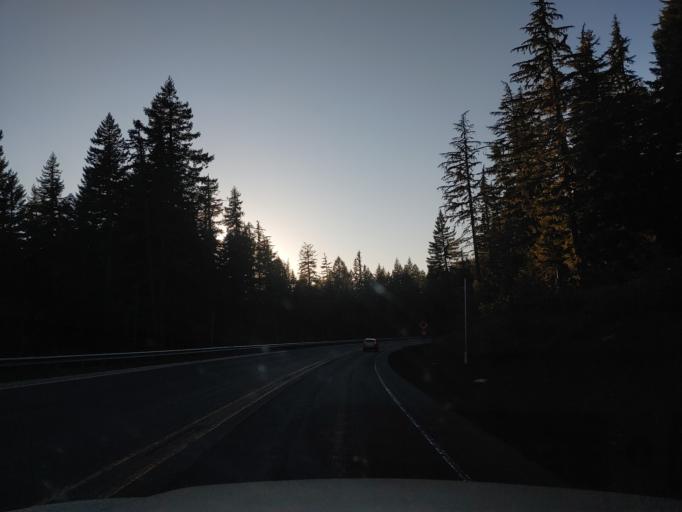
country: US
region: Oregon
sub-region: Lane County
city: Oakridge
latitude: 43.6110
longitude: -122.1229
